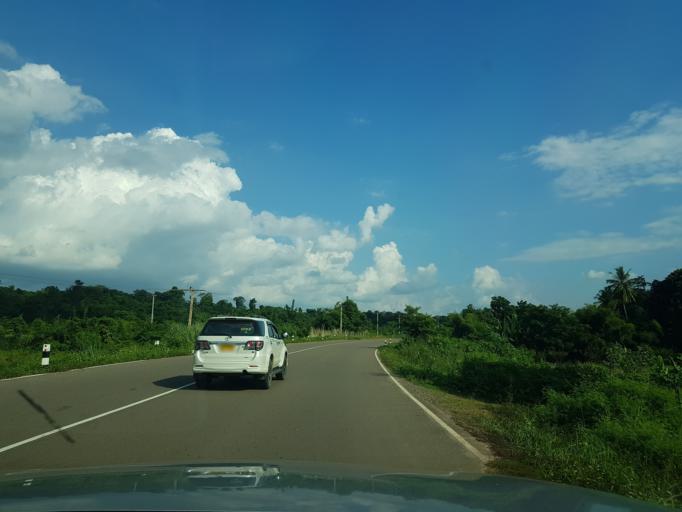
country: TH
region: Nong Khai
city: Pho Tak
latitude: 17.9941
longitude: 102.4192
